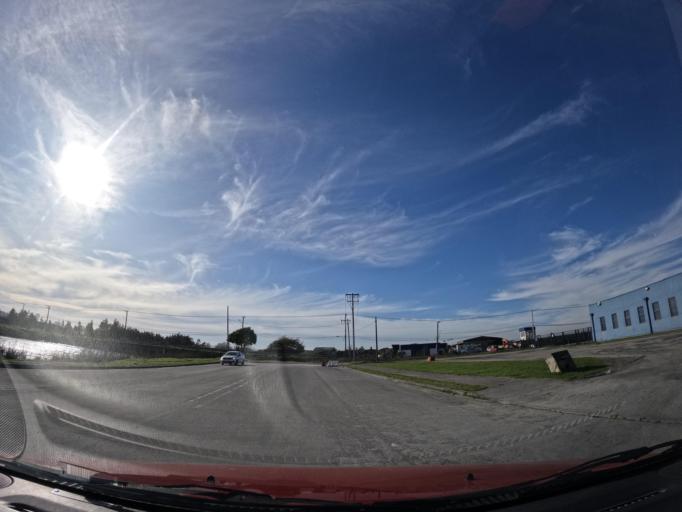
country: CL
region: Biobio
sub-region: Provincia de Concepcion
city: Talcahuano
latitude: -36.7678
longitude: -73.0747
